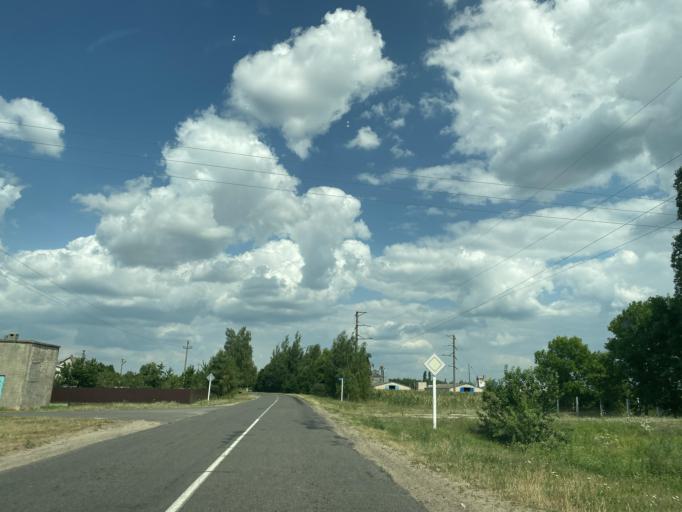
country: BY
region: Brest
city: Ivanava
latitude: 52.3471
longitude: 25.6284
